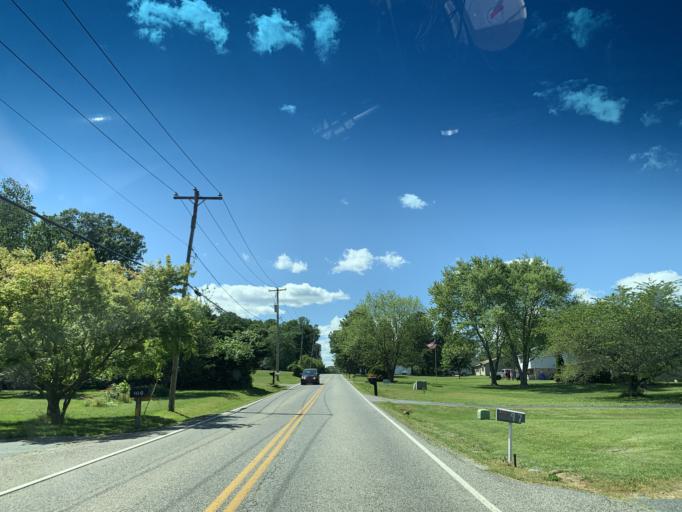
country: US
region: Maryland
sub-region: Cecil County
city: North East
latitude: 39.5608
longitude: -75.8848
